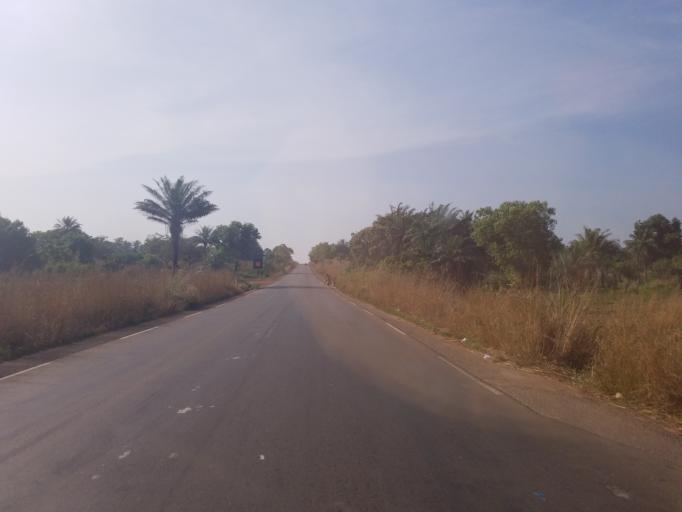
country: GN
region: Boke
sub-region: Boffa
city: Boffa
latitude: 10.1881
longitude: -14.0467
